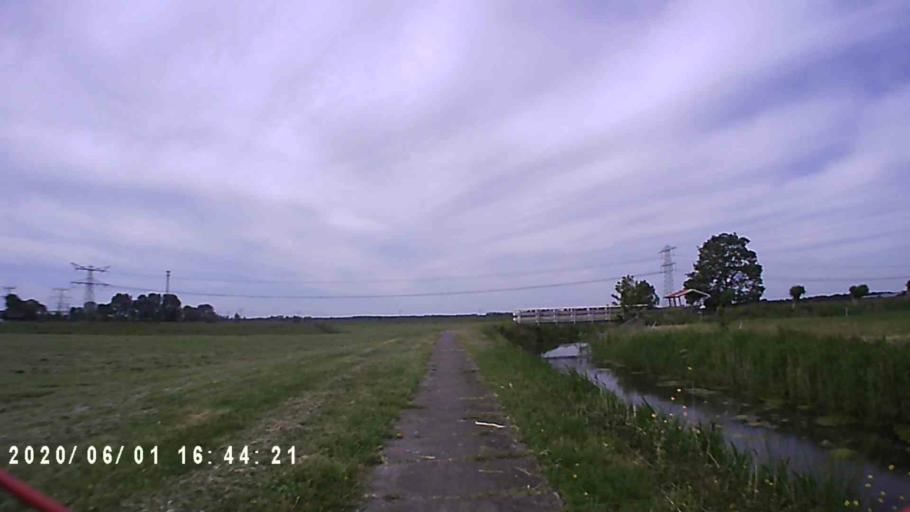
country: NL
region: Friesland
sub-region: Gemeente Boarnsterhim
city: Warten
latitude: 53.1849
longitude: 5.8832
